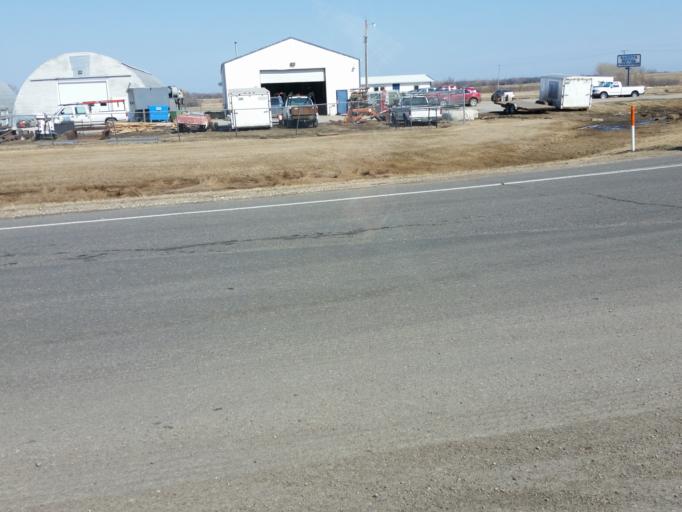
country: US
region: North Dakota
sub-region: Grand Forks County
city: Grand Forks
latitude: 48.0778
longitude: -97.1762
